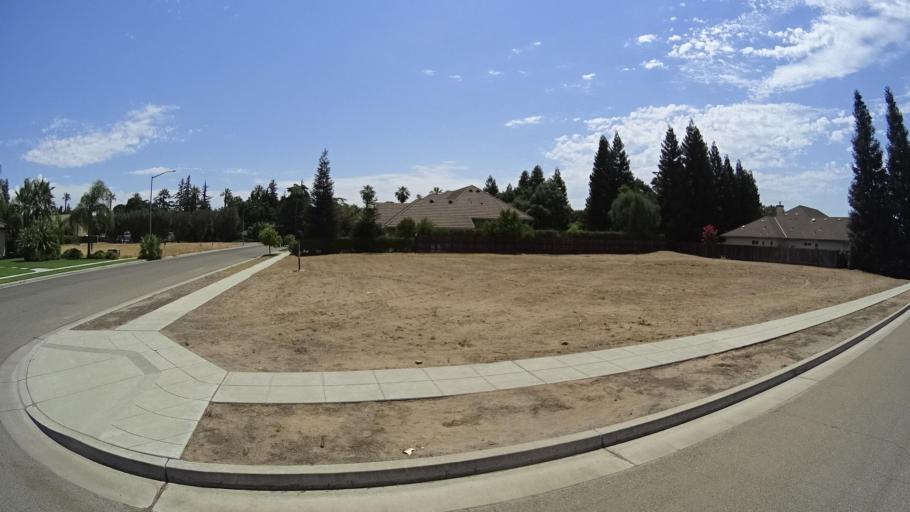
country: US
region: California
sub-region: Fresno County
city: Sunnyside
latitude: 36.7274
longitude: -119.7111
